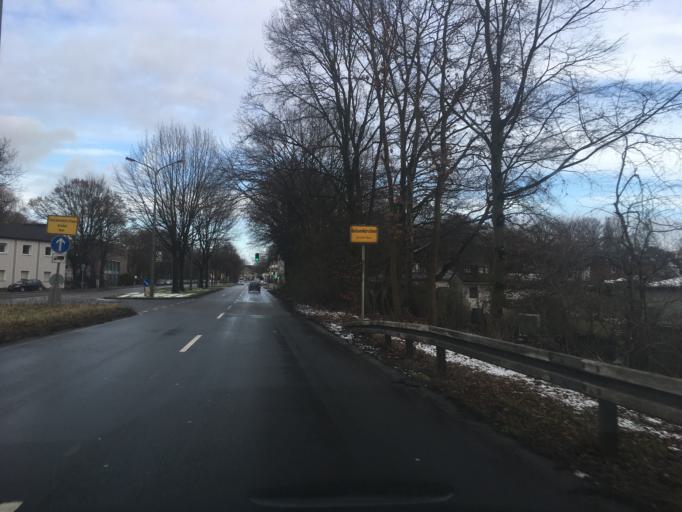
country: DE
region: North Rhine-Westphalia
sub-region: Regierungsbezirk Munster
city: Gladbeck
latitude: 51.5822
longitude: 7.0334
